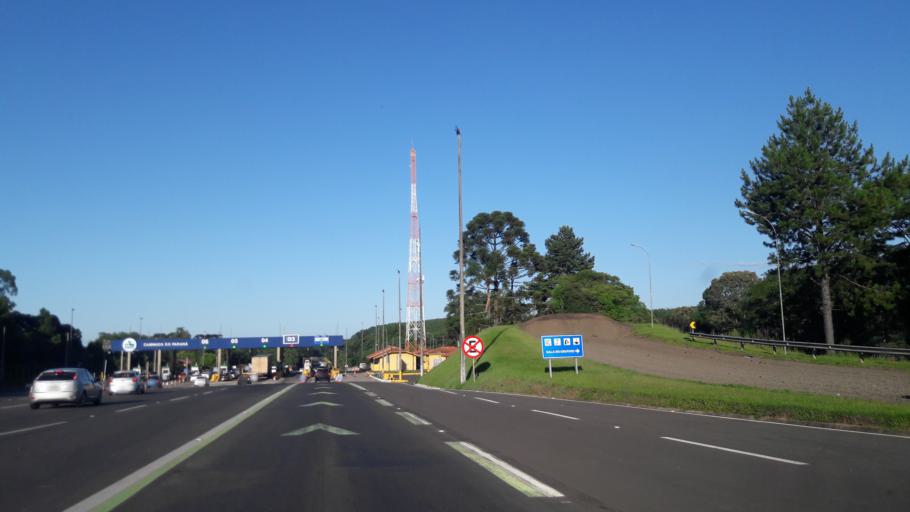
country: BR
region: Parana
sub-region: Prudentopolis
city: Prudentopolis
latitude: -25.3106
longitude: -51.1695
